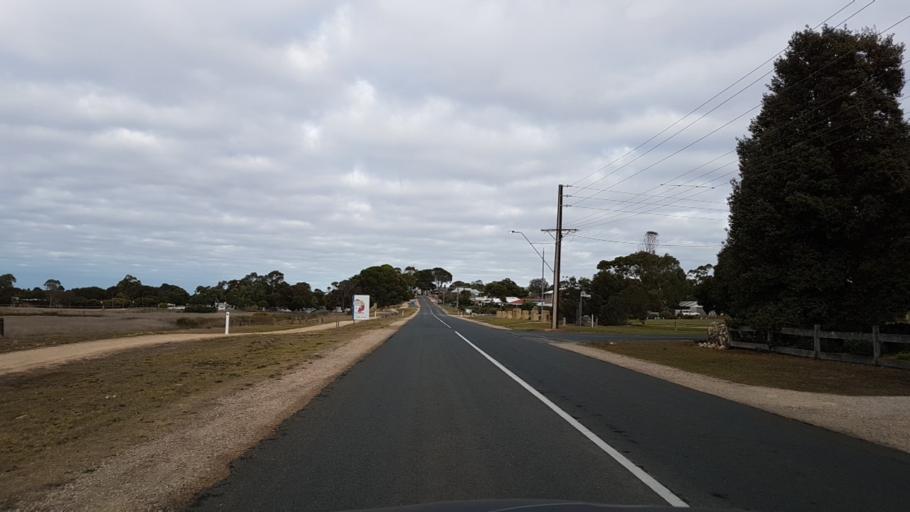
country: AU
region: South Australia
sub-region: Alexandrina
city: Langhorne Creek
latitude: -35.4038
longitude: 138.9784
